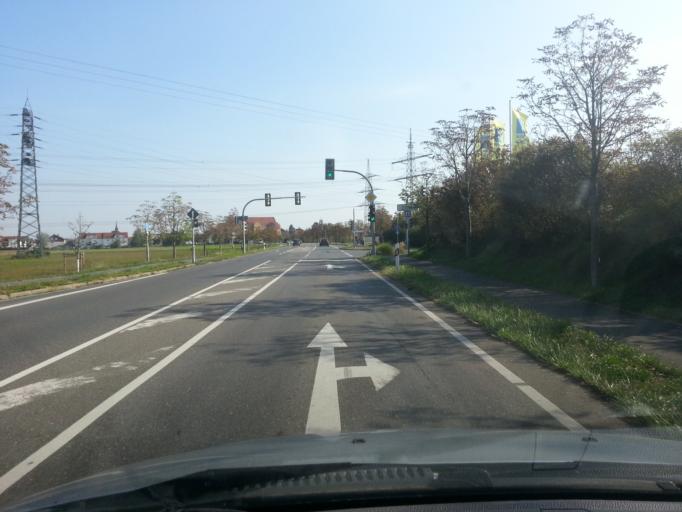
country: DE
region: Baden-Wuerttemberg
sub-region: Karlsruhe Region
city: Neulussheim
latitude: 49.2958
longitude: 8.5111
